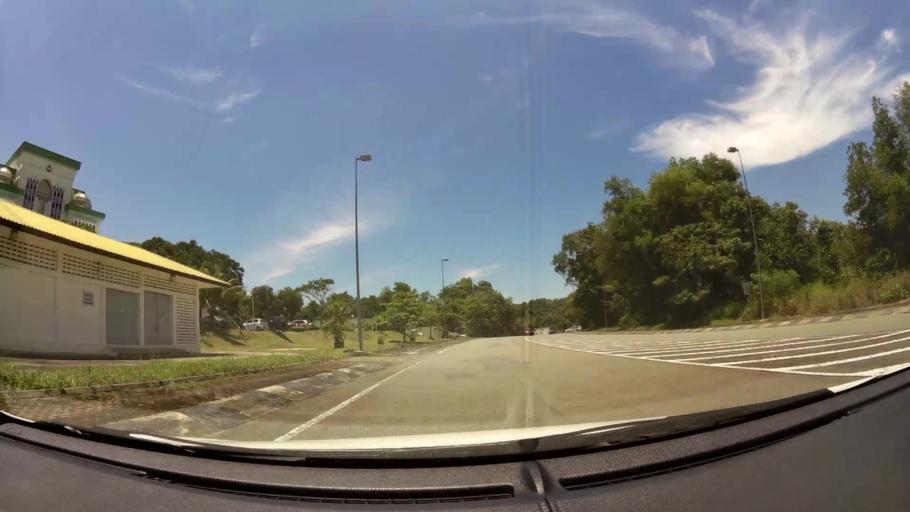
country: BN
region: Brunei and Muara
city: Bandar Seri Begawan
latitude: 4.9163
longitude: 114.9460
